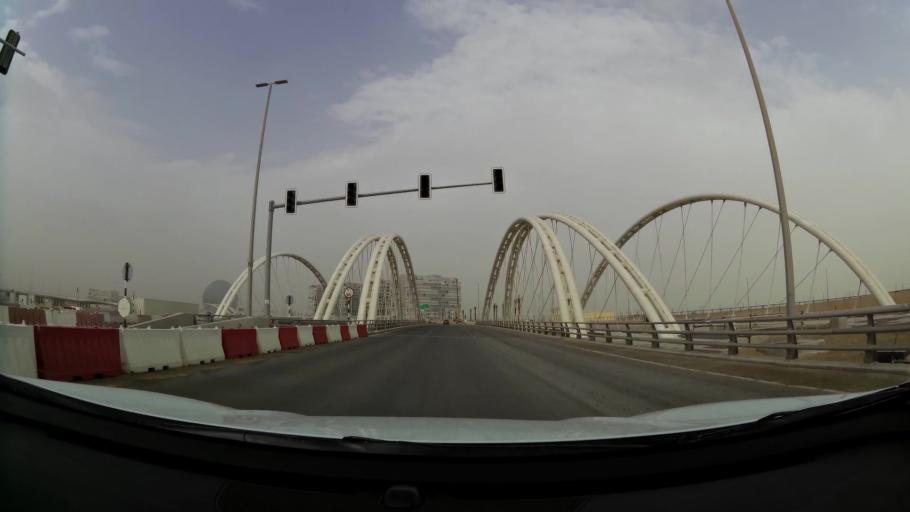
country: AE
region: Abu Dhabi
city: Abu Dhabi
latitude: 24.4451
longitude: 54.5893
